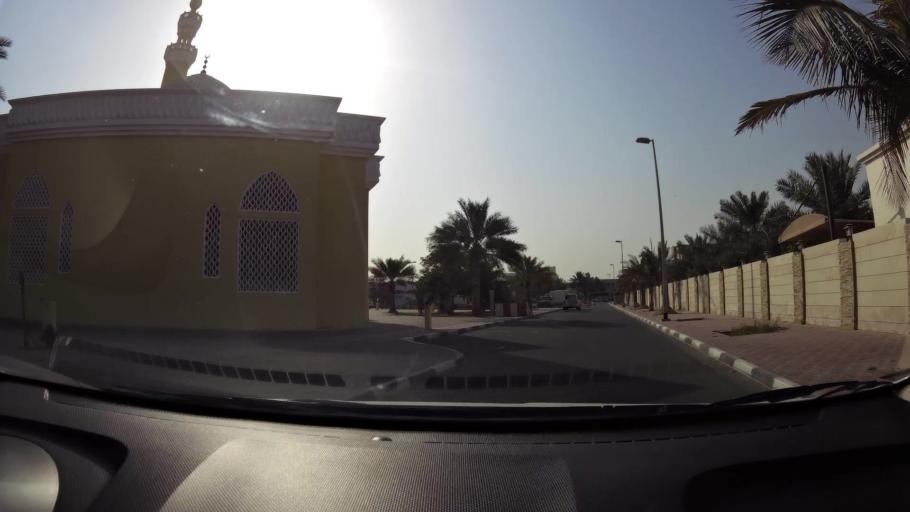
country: AE
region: Ash Shariqah
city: Sharjah
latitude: 25.3125
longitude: 55.3415
